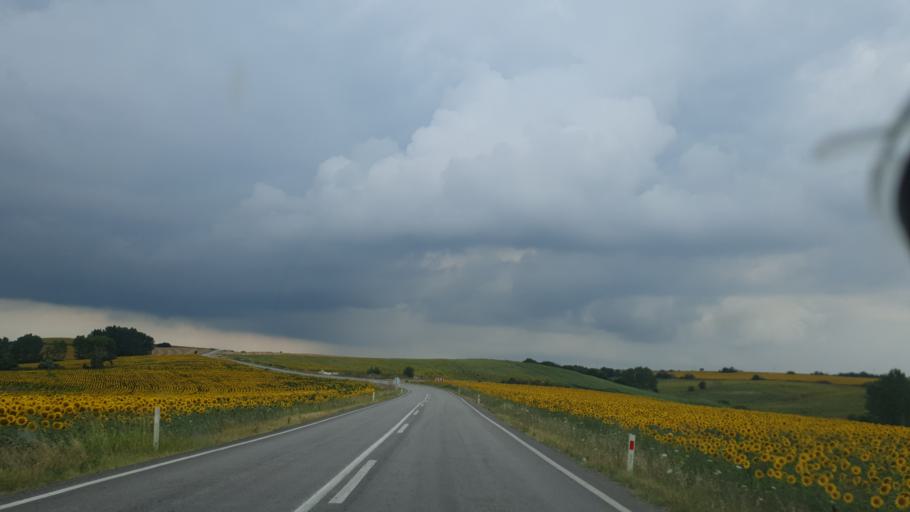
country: TR
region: Tekirdag
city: Hayrabolu
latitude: 41.2215
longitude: 27.0021
